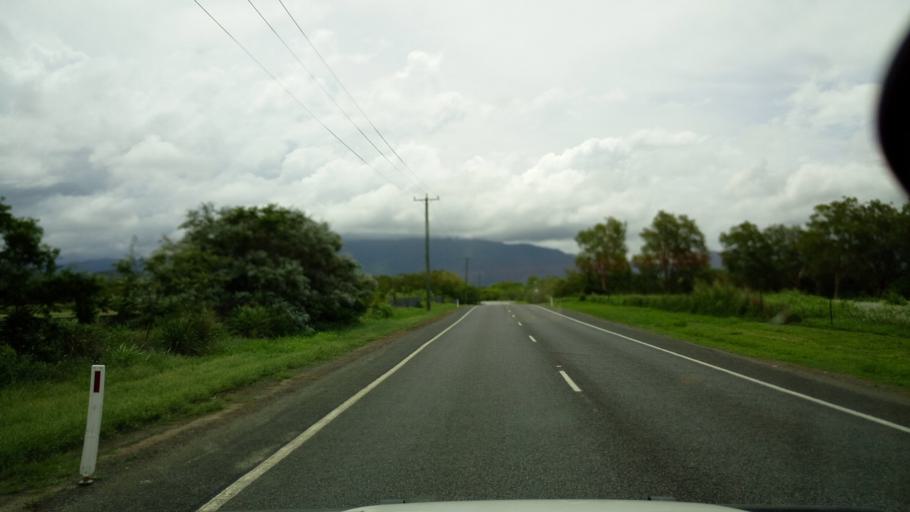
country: AU
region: Queensland
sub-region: Cairns
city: Redlynch
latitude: -16.8590
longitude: 145.7379
